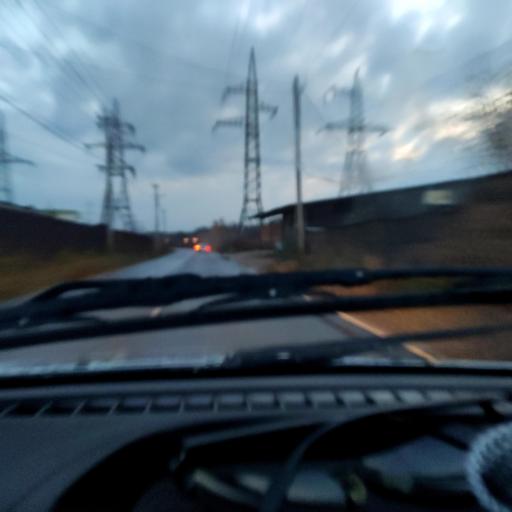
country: RU
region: Samara
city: Zhigulevsk
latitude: 53.5195
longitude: 49.4843
